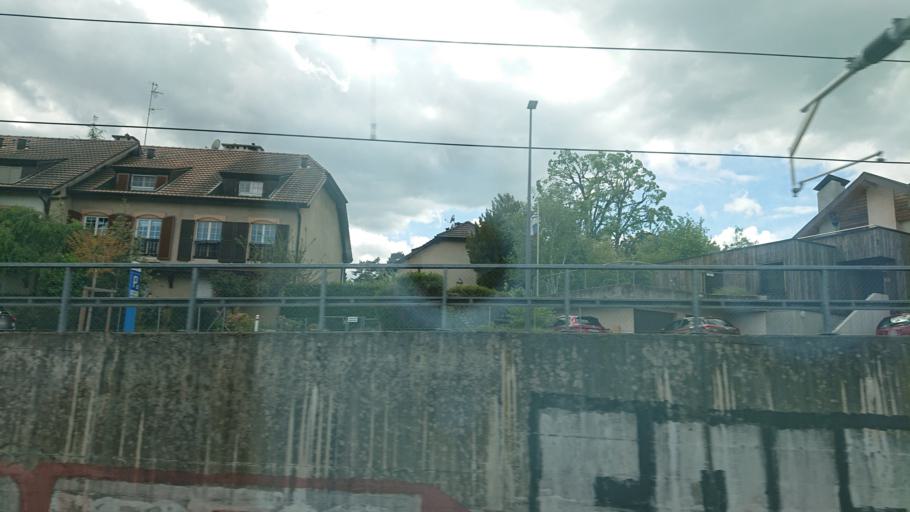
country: CH
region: Geneva
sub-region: Geneva
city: Versoix
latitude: 46.2838
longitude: 6.1633
